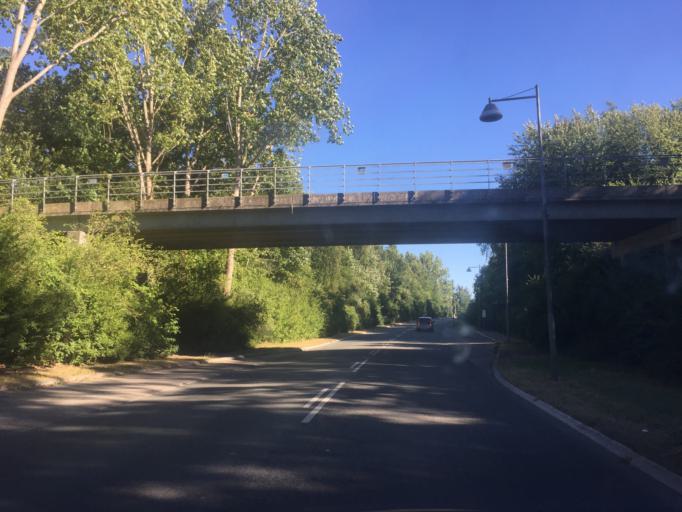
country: DK
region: Capital Region
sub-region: Albertslund Kommune
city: Albertslund
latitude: 55.6696
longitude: 12.3496
